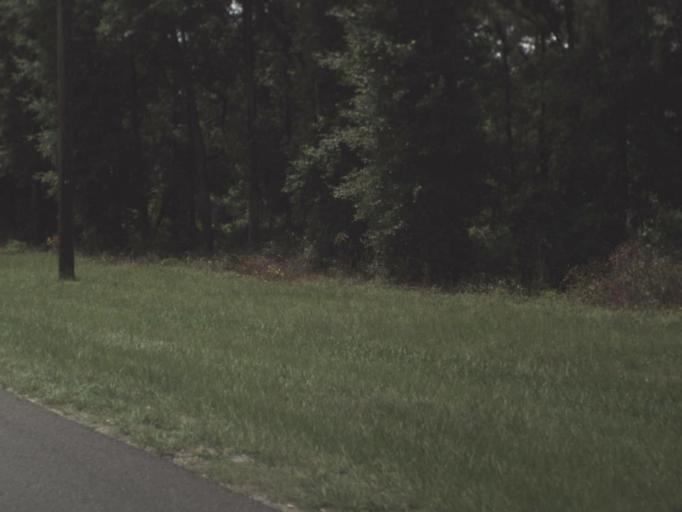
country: US
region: Florida
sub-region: Clay County
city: Keystone Heights
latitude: 29.8009
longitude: -82.0561
